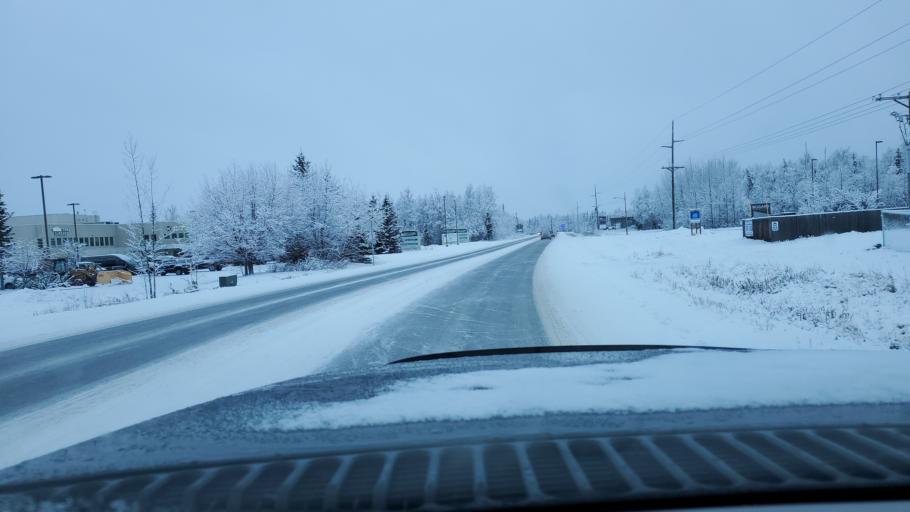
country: US
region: Alaska
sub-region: Matanuska-Susitna Borough
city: Wasilla
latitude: 61.5890
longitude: -149.4043
